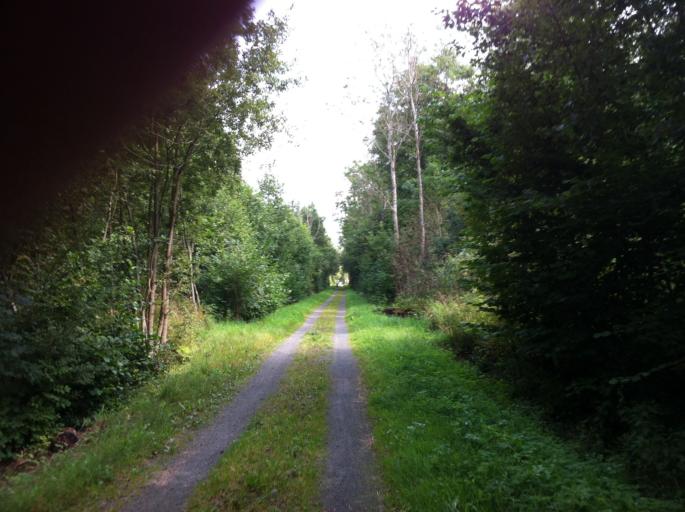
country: SE
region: Skane
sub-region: Kristianstads Kommun
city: Onnestad
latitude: 55.9413
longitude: 13.9138
